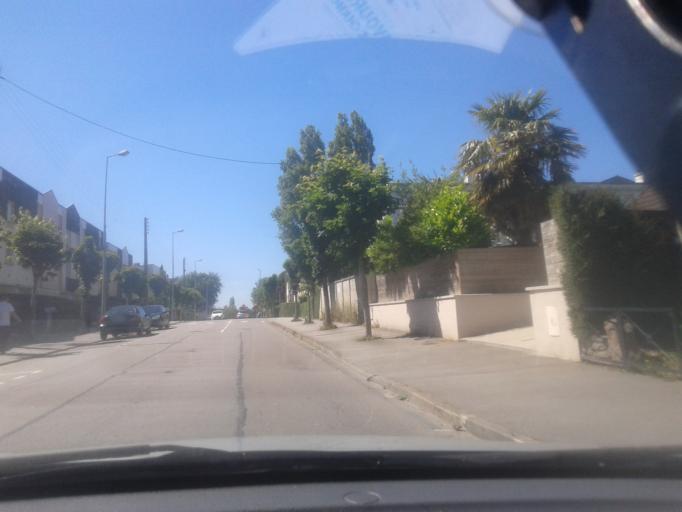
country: FR
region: Lower Normandy
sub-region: Departement de la Manche
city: Octeville
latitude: 49.6298
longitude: -1.6428
